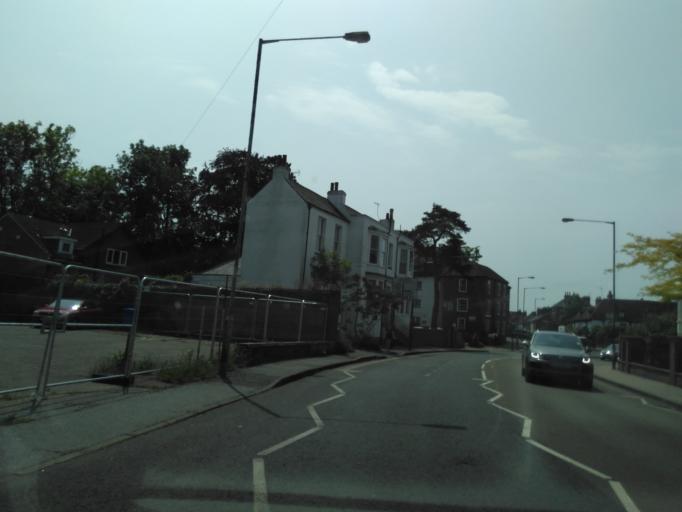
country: GB
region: England
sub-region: Kent
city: Canterbury
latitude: 51.2844
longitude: 1.0798
